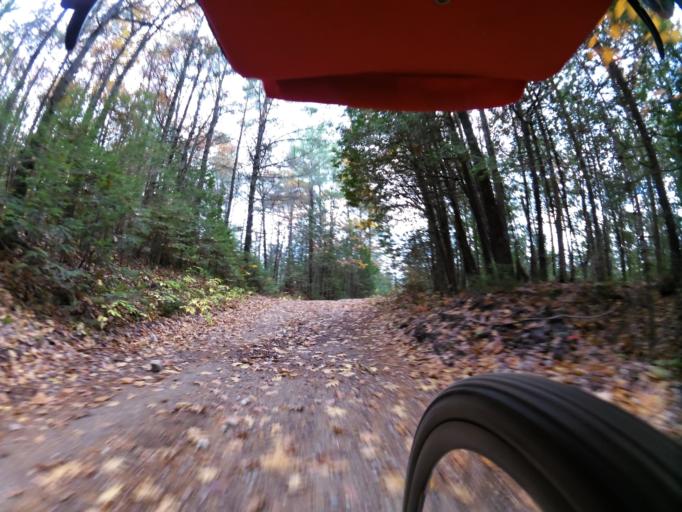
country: CA
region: Ontario
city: Arnprior
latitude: 45.6549
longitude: -76.2094
